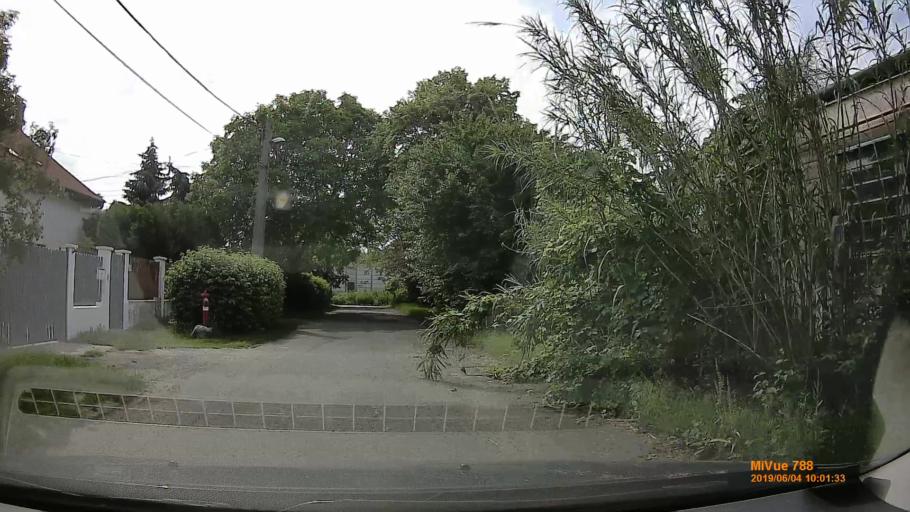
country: HU
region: Pest
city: Halasztelek
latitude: 47.3938
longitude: 18.9950
